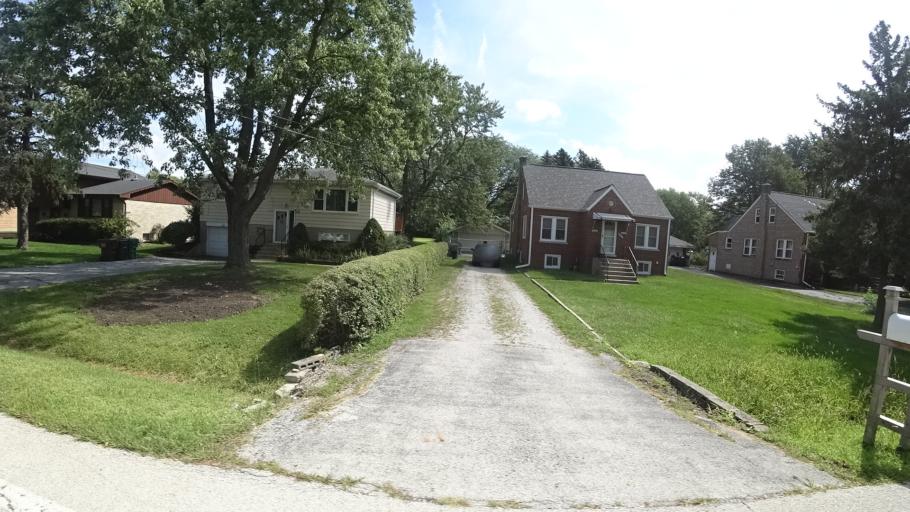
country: US
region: Illinois
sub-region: Cook County
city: Tinley Park
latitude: 41.5718
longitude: -87.7745
